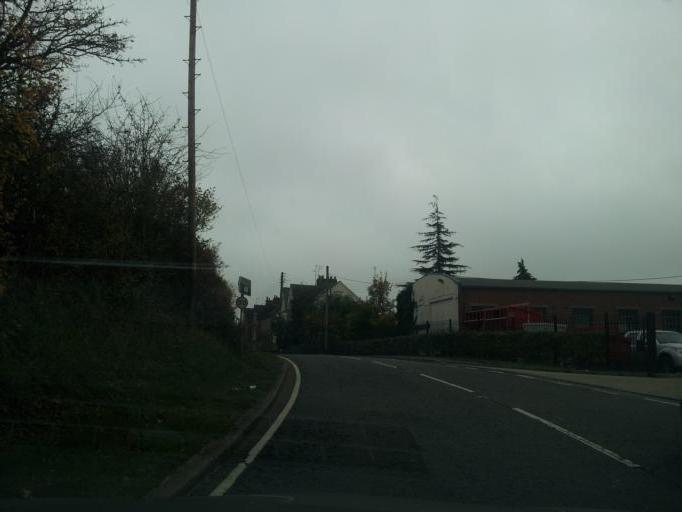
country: GB
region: England
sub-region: Buckinghamshire
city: Buckingham
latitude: 52.0017
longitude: -0.9986
